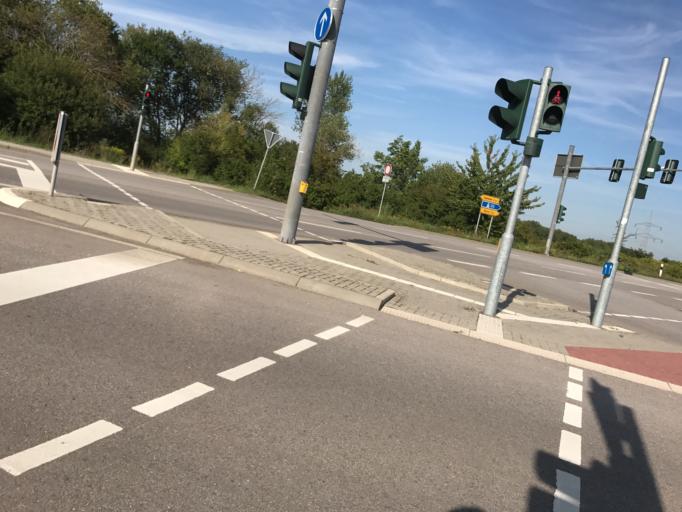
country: DE
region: Rheinland-Pfalz
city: Budenheim
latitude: 50.0281
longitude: 8.1947
